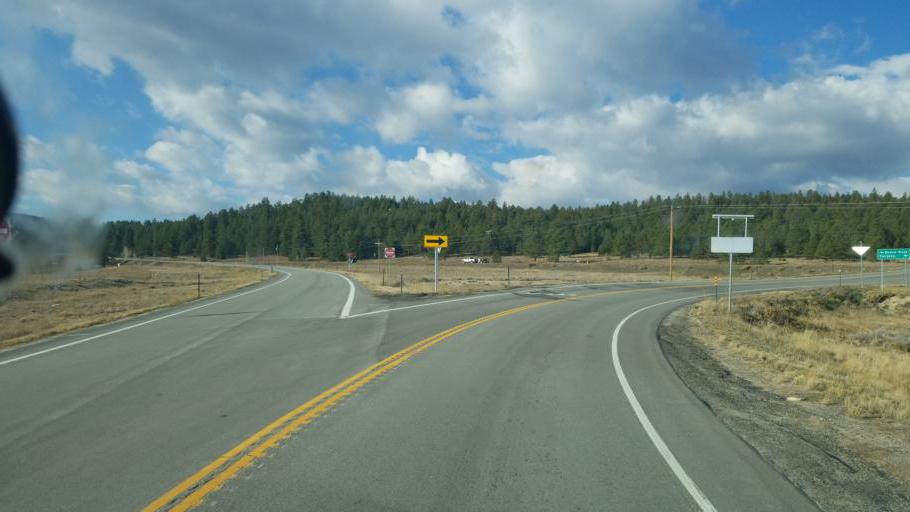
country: US
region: Colorado
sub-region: Chaffee County
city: Buena Vista
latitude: 38.9222
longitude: -105.9665
